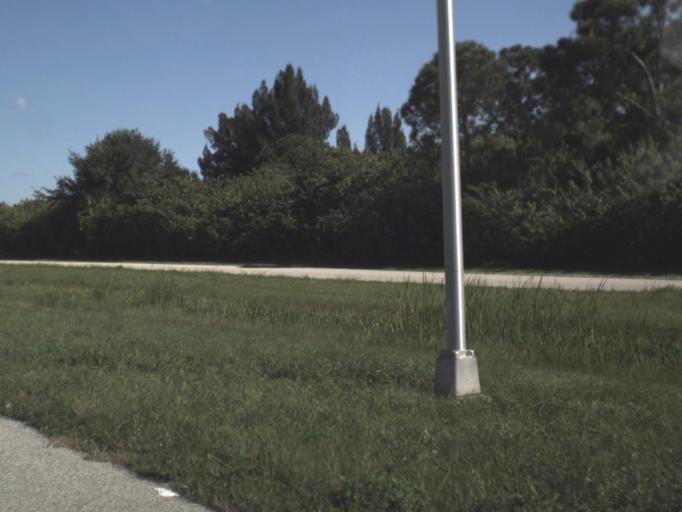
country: US
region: Florida
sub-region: Charlotte County
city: Rotonda
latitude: 26.9326
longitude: -82.2548
